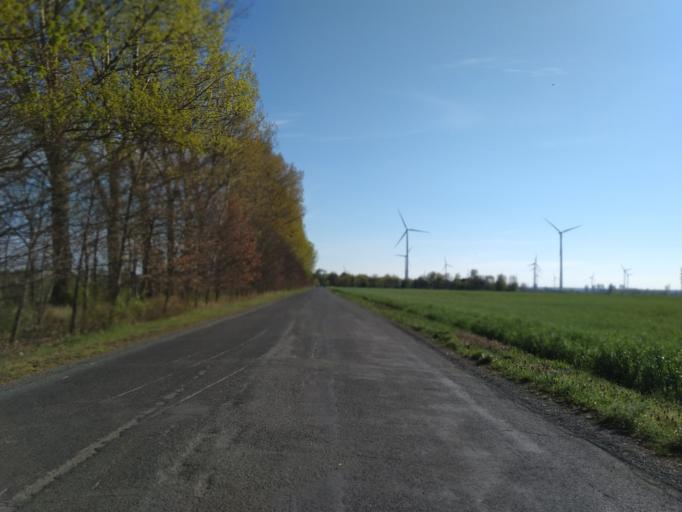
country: DE
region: Brandenburg
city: Neutrebbin
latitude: 52.7206
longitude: 14.2125
